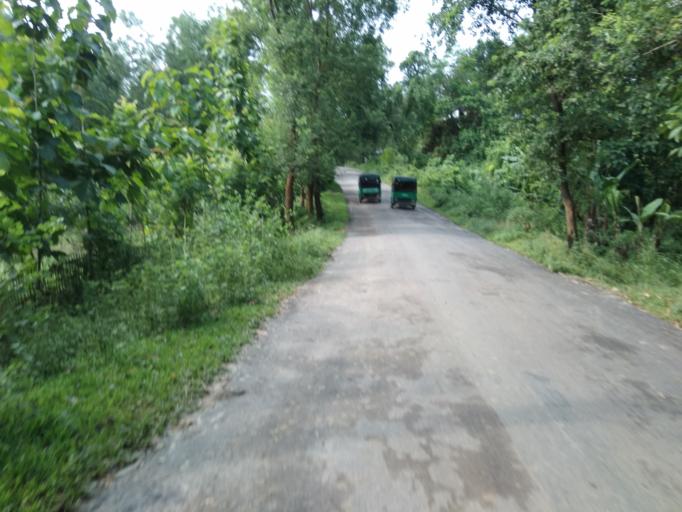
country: BD
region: Chittagong
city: Khagrachhari
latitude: 23.0048
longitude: 92.0112
